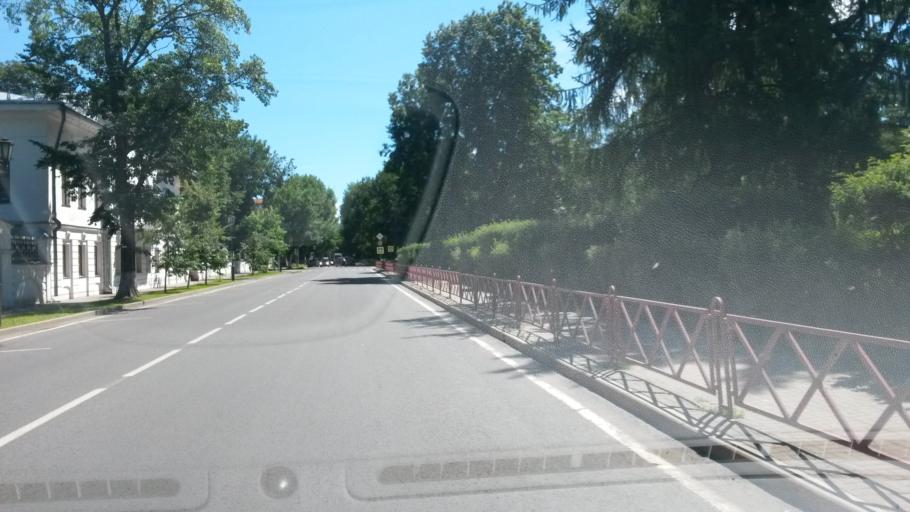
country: RU
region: Jaroslavl
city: Yaroslavl
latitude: 57.6273
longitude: 39.8949
